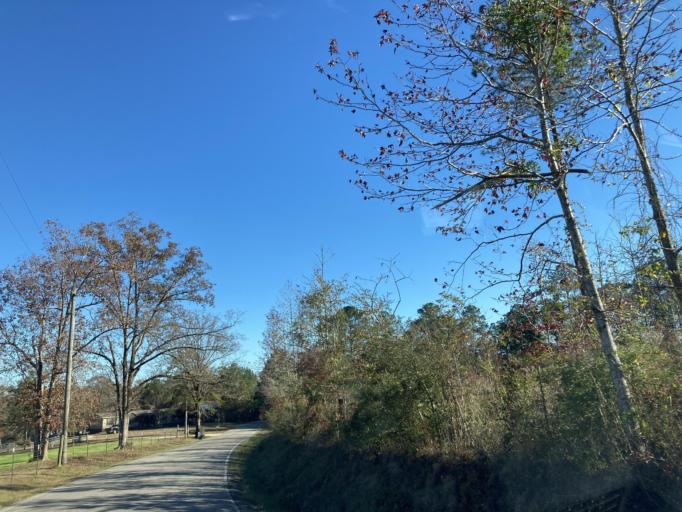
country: US
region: Mississippi
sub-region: Lamar County
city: Sumrall
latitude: 31.3712
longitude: -89.5816
